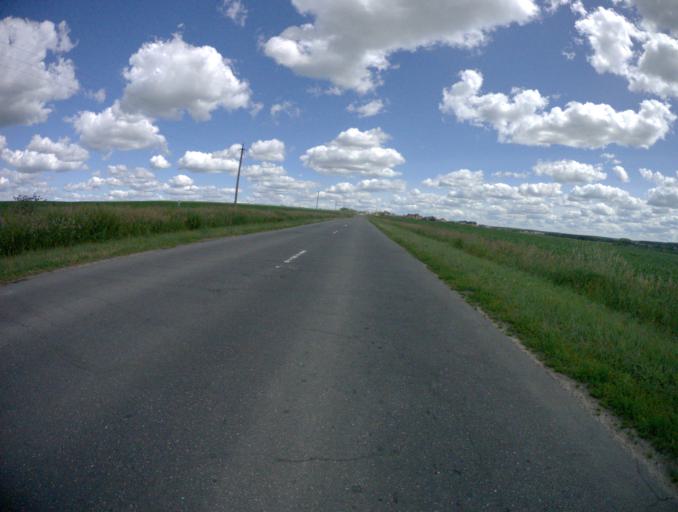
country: RU
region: Vladimir
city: Bogolyubovo
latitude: 56.2921
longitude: 40.5461
